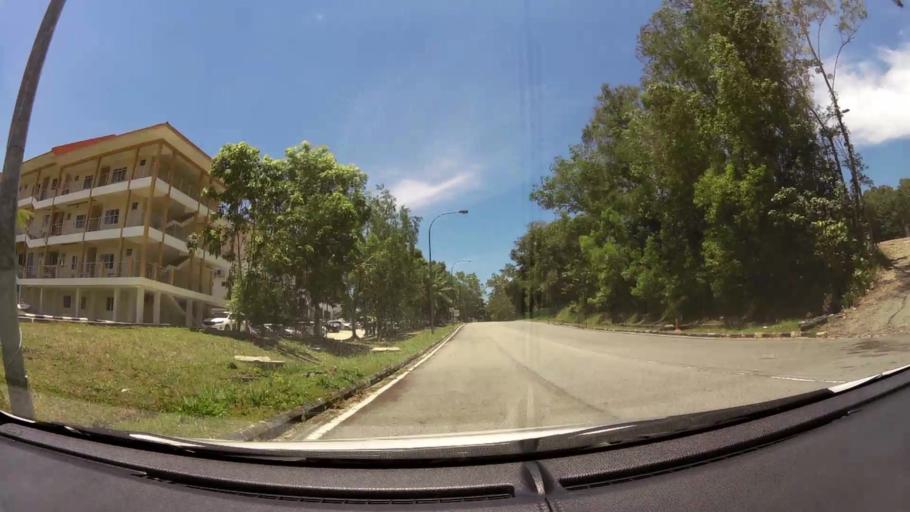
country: BN
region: Brunei and Muara
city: Bandar Seri Begawan
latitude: 4.9246
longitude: 114.9619
